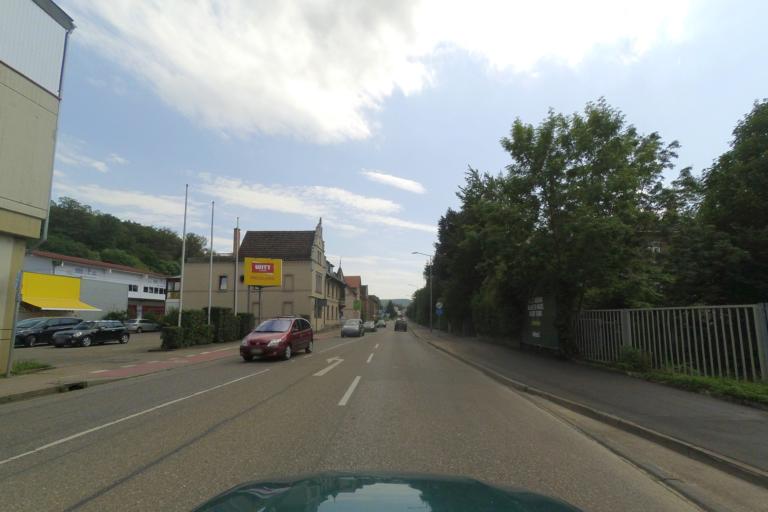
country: DE
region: Baden-Wuerttemberg
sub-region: Regierungsbezirk Stuttgart
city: Aalen
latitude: 48.8559
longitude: 10.1011
